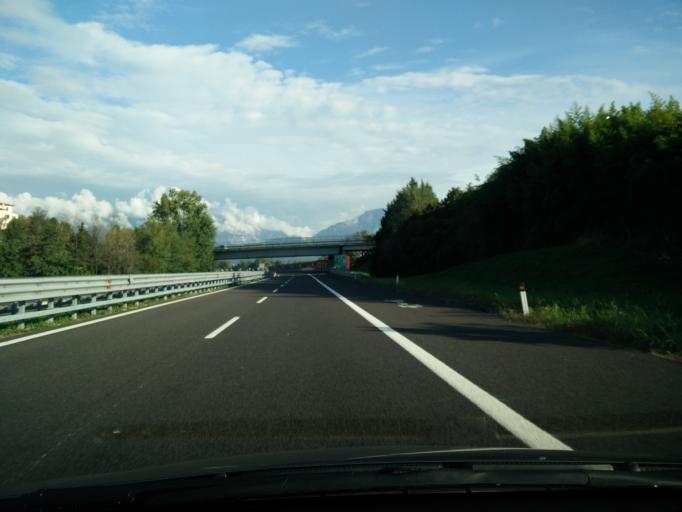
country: IT
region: Veneto
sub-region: Provincia di Treviso
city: Scomigo
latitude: 45.9317
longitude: 12.3131
